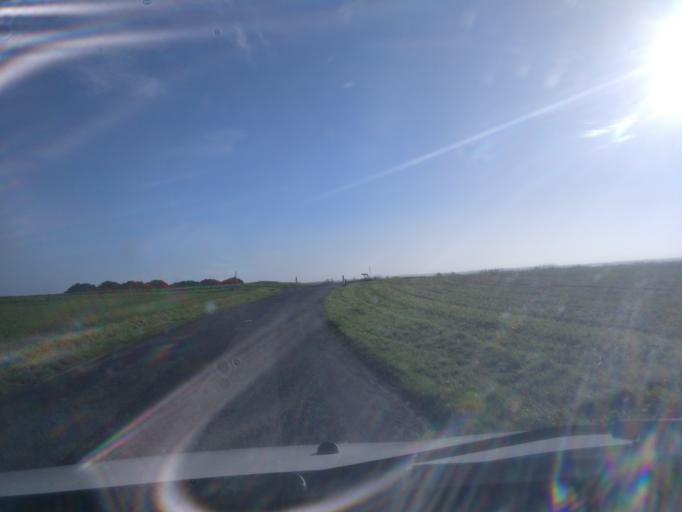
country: FR
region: Brittany
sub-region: Departement d'Ille-et-Vilaine
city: Pleine-Fougeres
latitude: 48.5337
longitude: -1.5440
